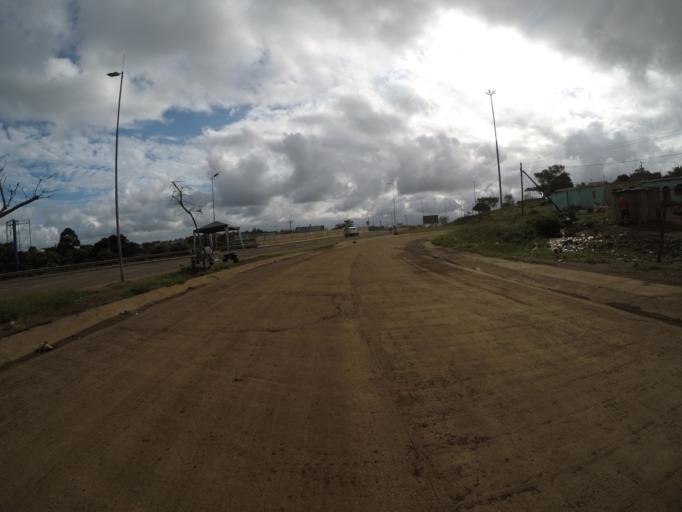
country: ZA
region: KwaZulu-Natal
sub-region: uMkhanyakude District Municipality
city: Mtubatuba
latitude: -28.4165
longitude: 32.1627
